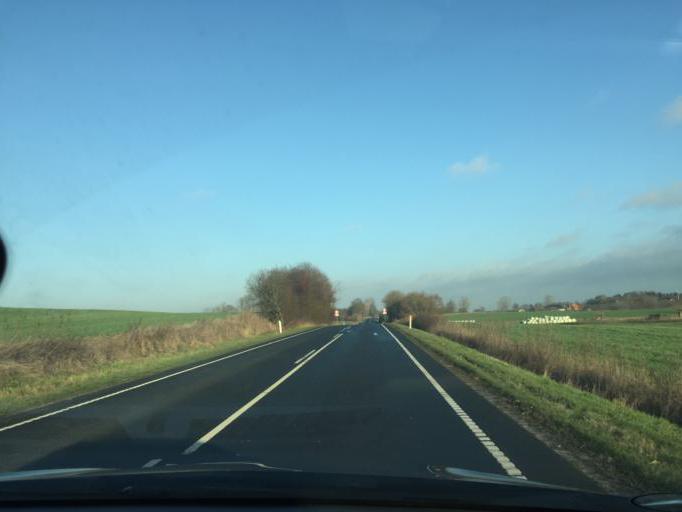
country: DK
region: South Denmark
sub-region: Faaborg-Midtfyn Kommune
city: Faaborg
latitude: 55.1752
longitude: 10.2919
